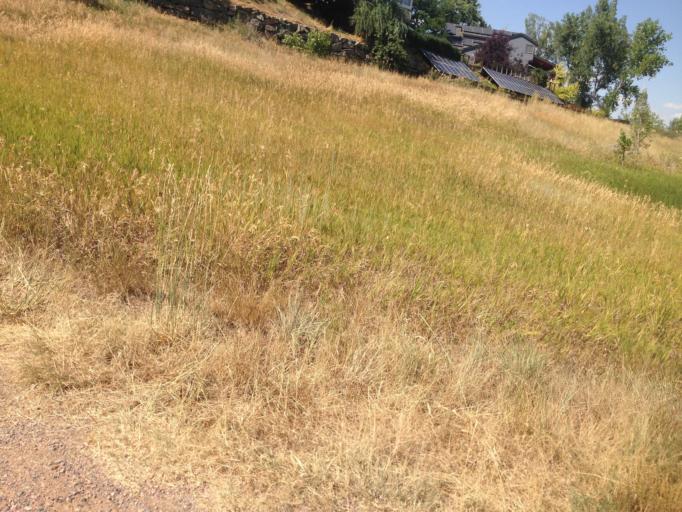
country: US
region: Colorado
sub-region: Boulder County
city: Louisville
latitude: 39.9833
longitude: -105.1487
